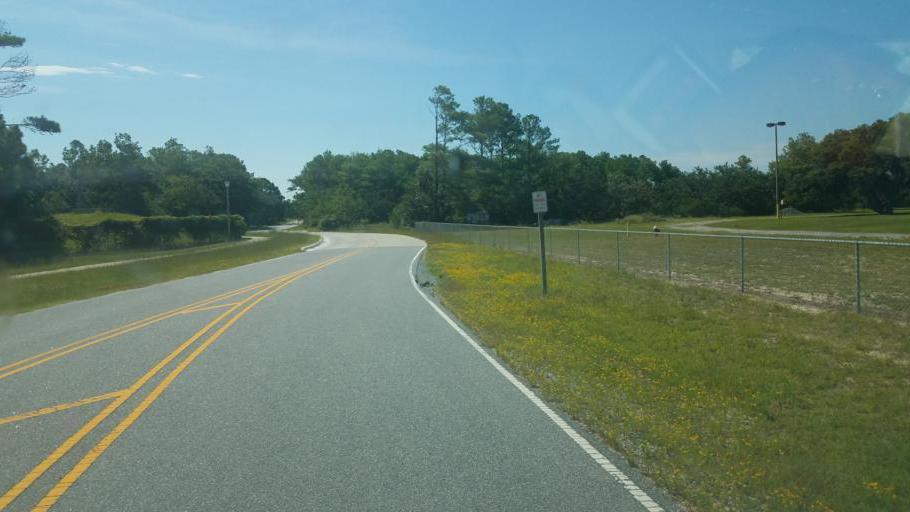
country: US
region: North Carolina
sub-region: Dare County
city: Kill Devil Hills
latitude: 36.0070
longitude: -75.6633
